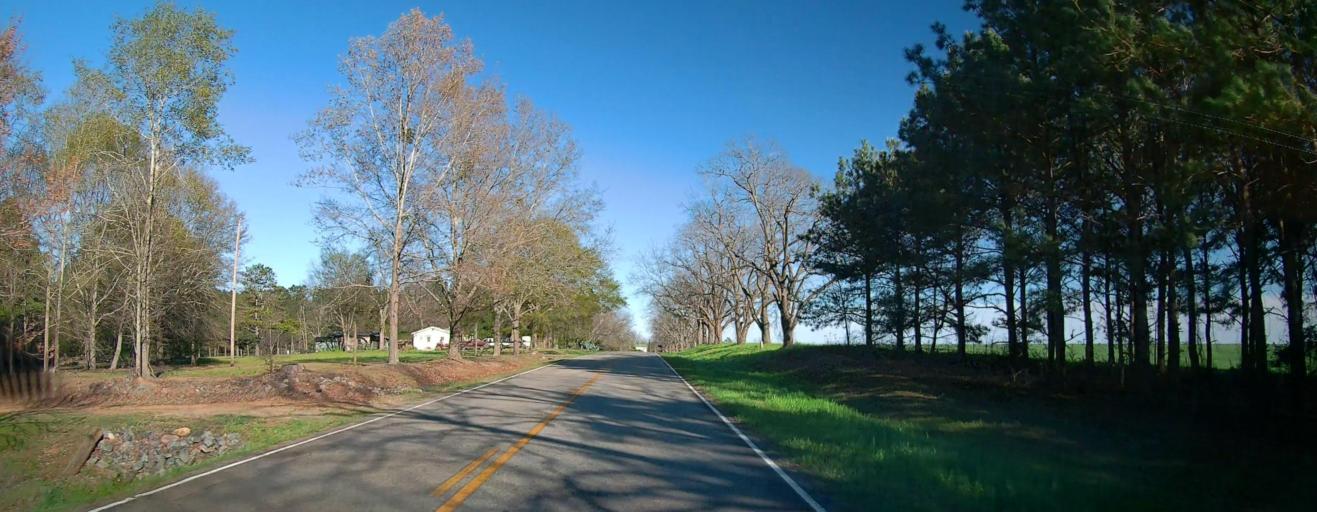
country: US
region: Georgia
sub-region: Houston County
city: Perry
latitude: 32.3740
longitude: -83.7137
